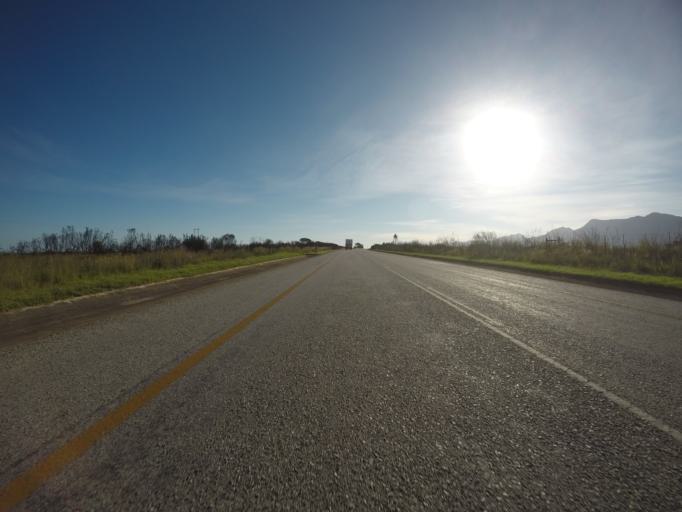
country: ZA
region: Eastern Cape
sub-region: Cacadu District Municipality
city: Kareedouw
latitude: -34.0470
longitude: 24.4170
